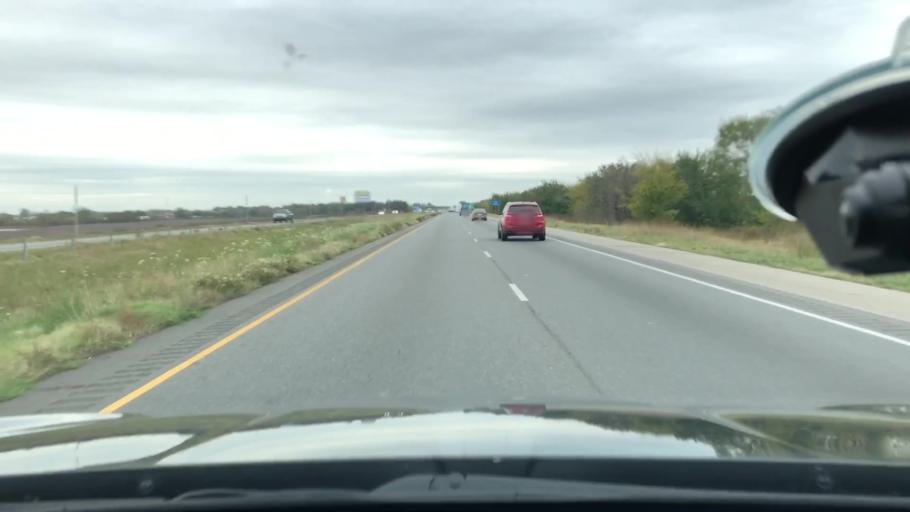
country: US
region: Arkansas
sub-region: Miller County
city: Texarkana
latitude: 33.5036
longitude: -93.9541
